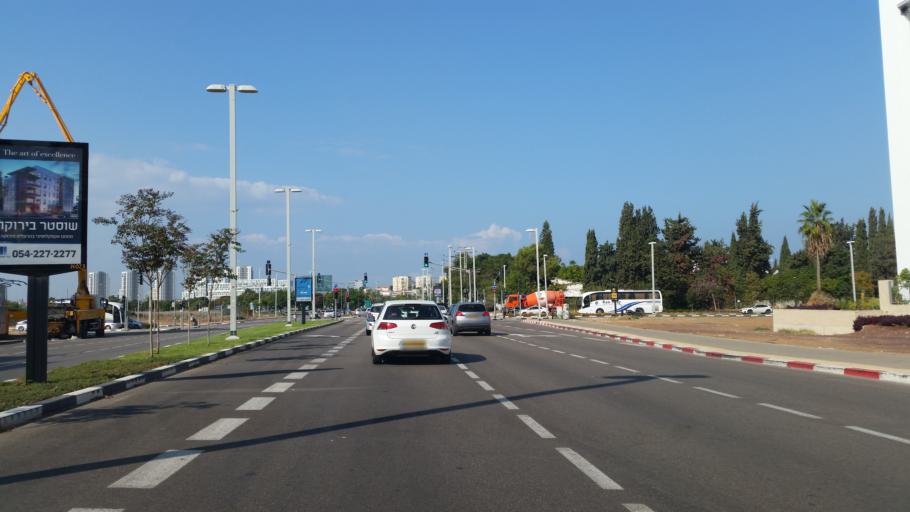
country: IL
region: Tel Aviv
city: Herzliyya
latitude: 32.1633
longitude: 34.8283
